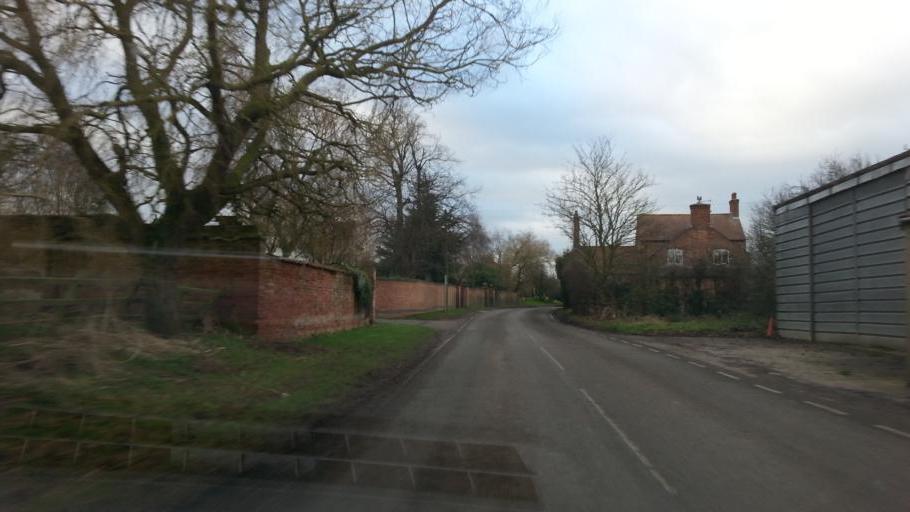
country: GB
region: England
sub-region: Nottinghamshire
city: Southwell
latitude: 53.1213
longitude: -0.8948
